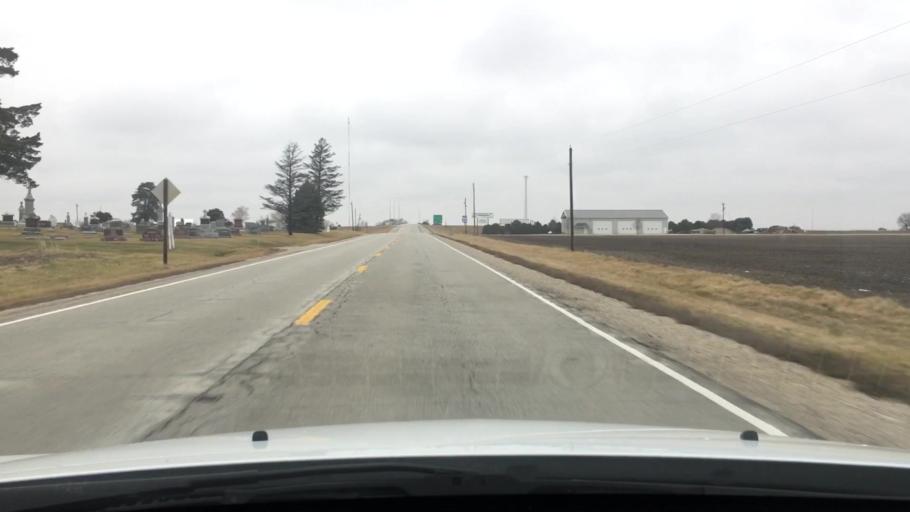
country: US
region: Illinois
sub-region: Iroquois County
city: Clifton
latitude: 40.8844
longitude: -87.9593
